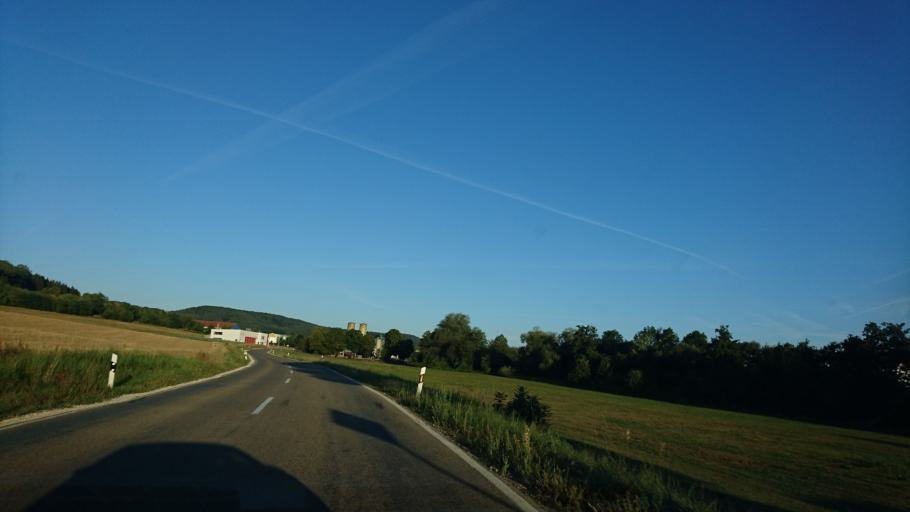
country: DE
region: Bavaria
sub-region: Regierungsbezirk Mittelfranken
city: Thalmassing
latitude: 49.0868
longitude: 11.2345
